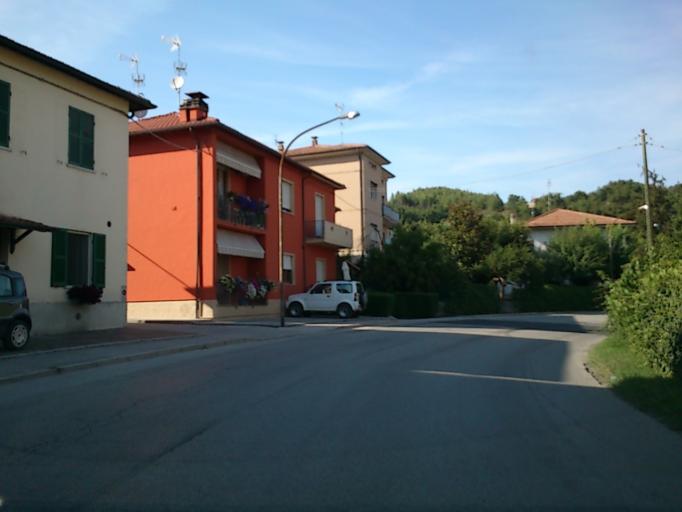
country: IT
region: The Marches
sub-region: Provincia di Pesaro e Urbino
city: Fermignano
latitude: 43.6901
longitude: 12.6426
